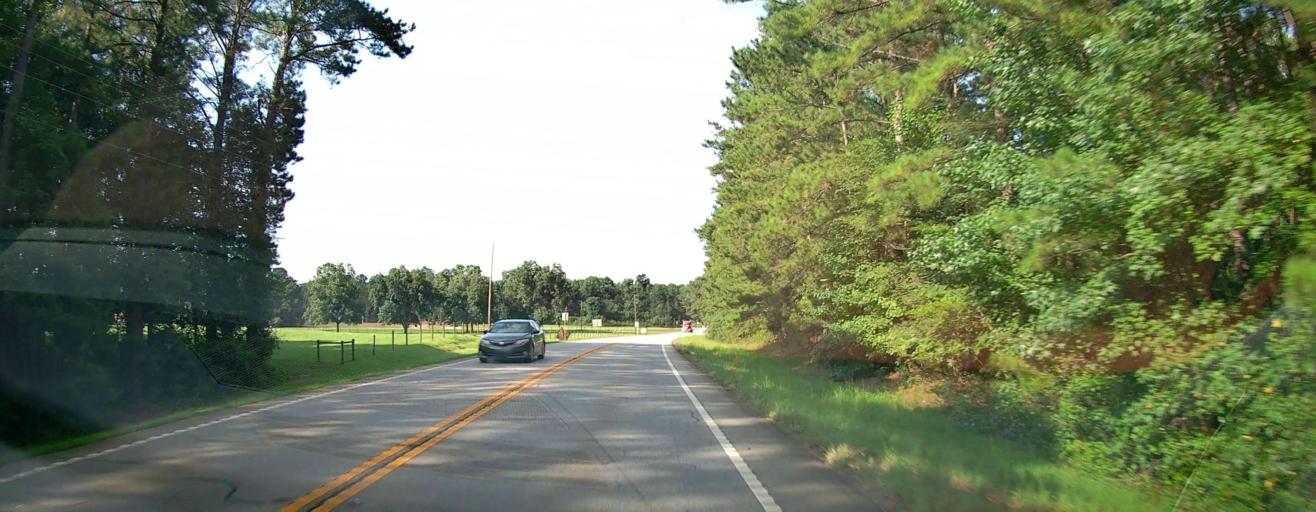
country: US
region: Georgia
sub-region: Coweta County
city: Senoia
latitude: 33.2192
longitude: -84.5774
